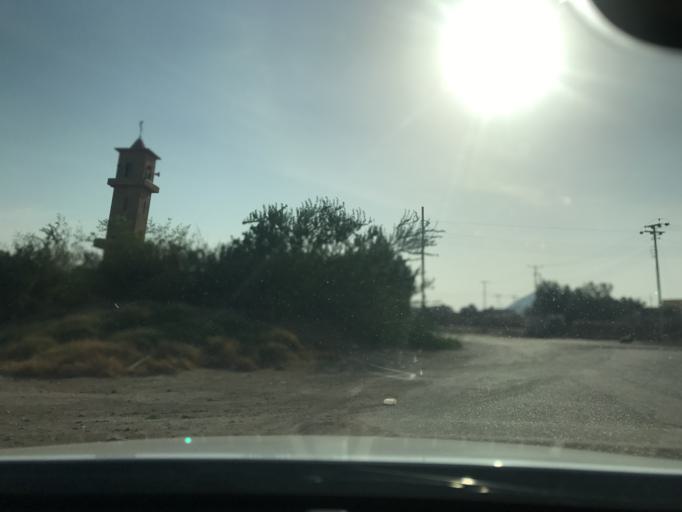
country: SA
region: Makkah
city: Al Jumum
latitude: 21.4368
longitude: 39.5219
